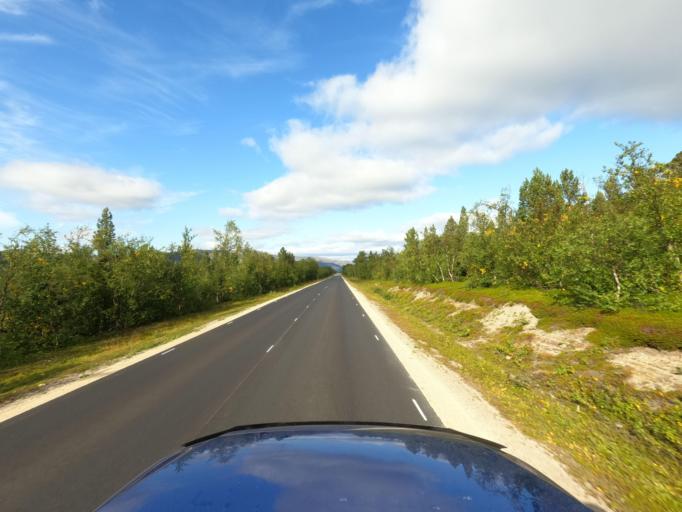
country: NO
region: Finnmark Fylke
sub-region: Porsanger
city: Lakselv
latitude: 69.9768
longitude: 24.9639
